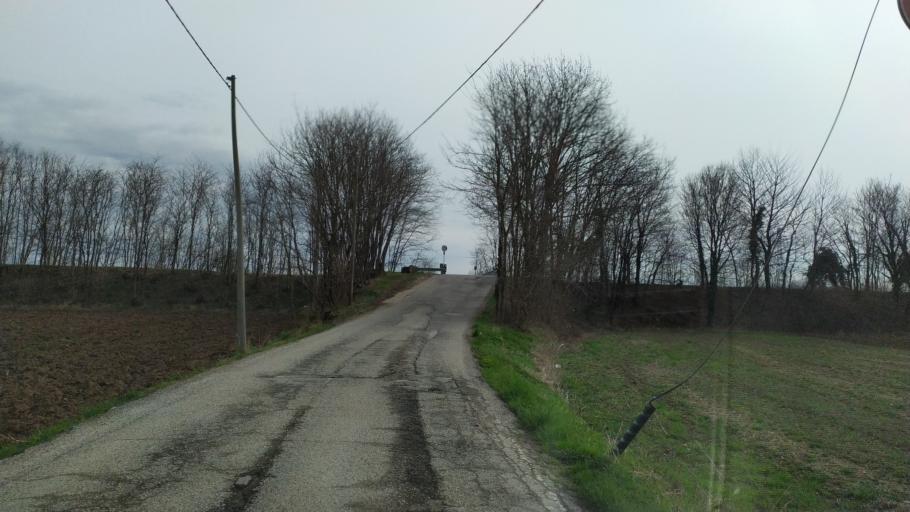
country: IT
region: Veneto
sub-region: Provincia di Vicenza
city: Isola Vicentina
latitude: 45.6545
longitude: 11.4520
